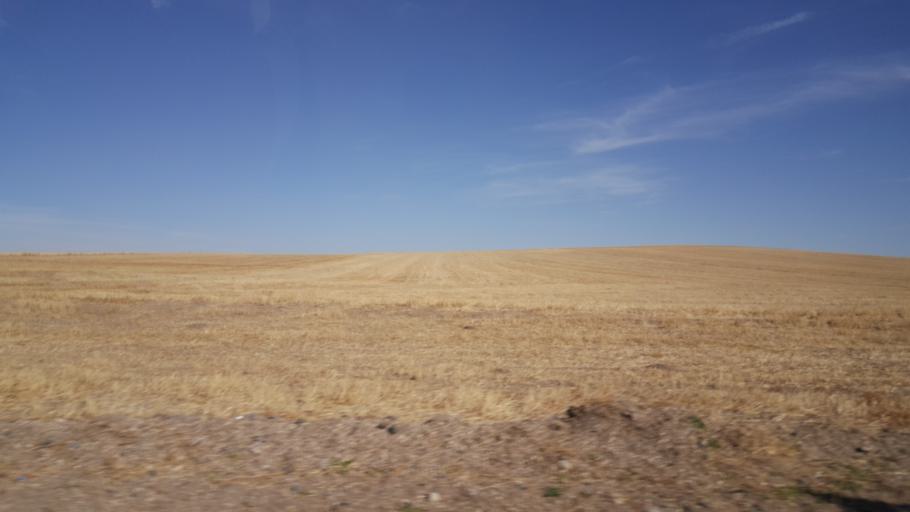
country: TR
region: Ankara
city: Yenice
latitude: 39.3222
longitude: 32.7552
